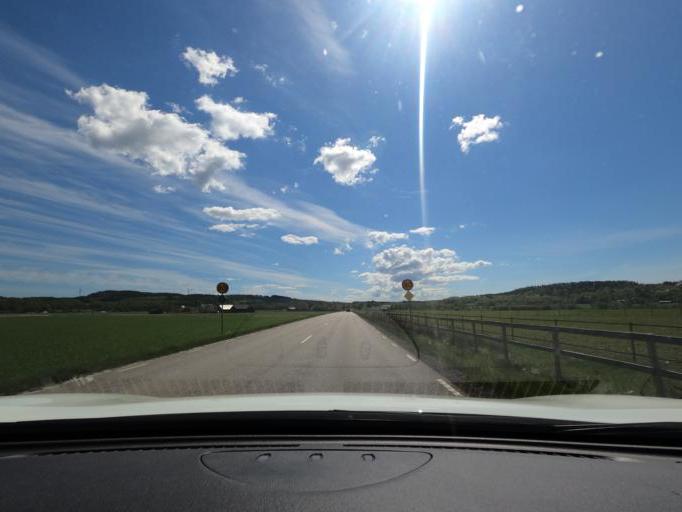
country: SE
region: Halland
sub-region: Kungsbacka Kommun
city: Fjaeras kyrkby
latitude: 57.4282
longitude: 12.1909
